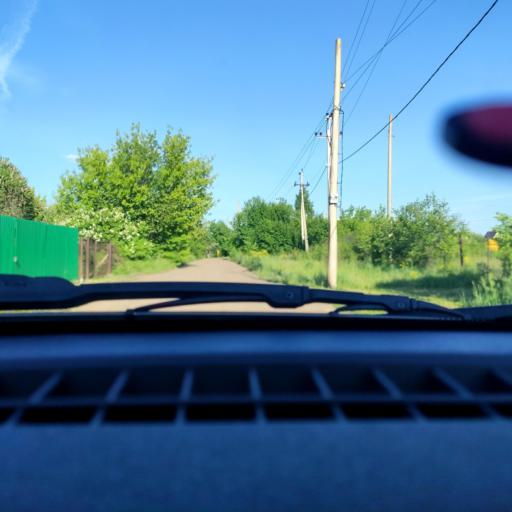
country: RU
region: Bashkortostan
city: Avdon
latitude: 54.4655
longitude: 55.8207
